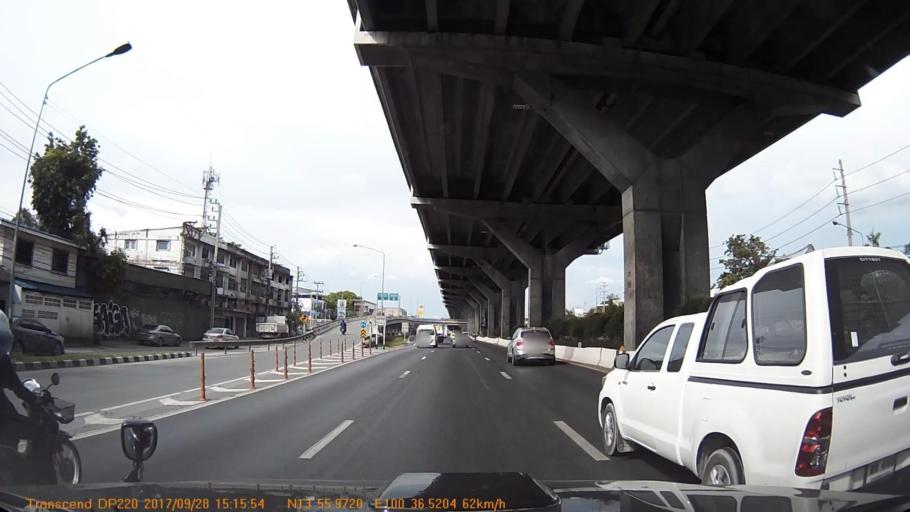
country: TH
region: Bangkok
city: Don Mueang
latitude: 13.9333
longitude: 100.6089
